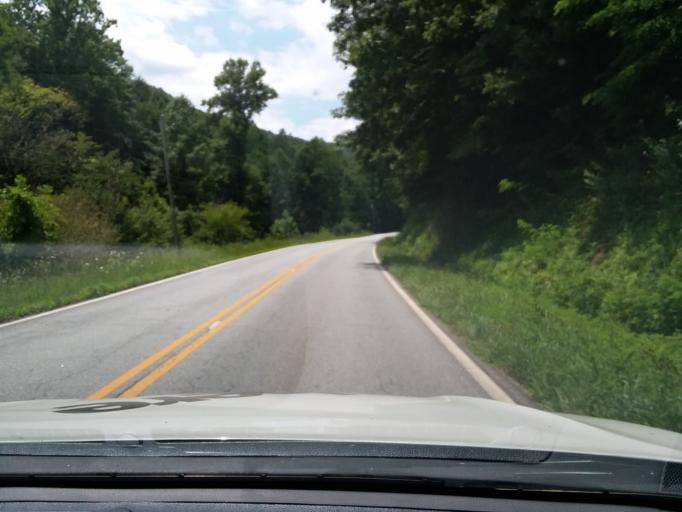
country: US
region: Georgia
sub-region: Rabun County
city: Mountain City
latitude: 34.8838
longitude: -83.3445
